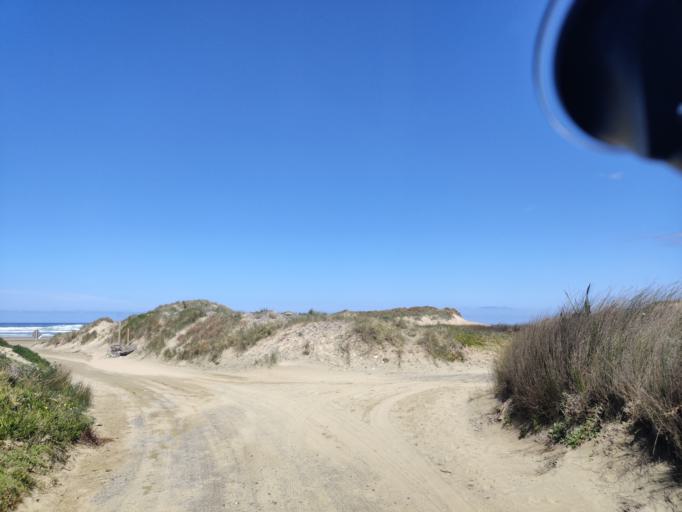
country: NZ
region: Northland
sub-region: Far North District
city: Kaitaia
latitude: -34.8982
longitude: 173.0856
